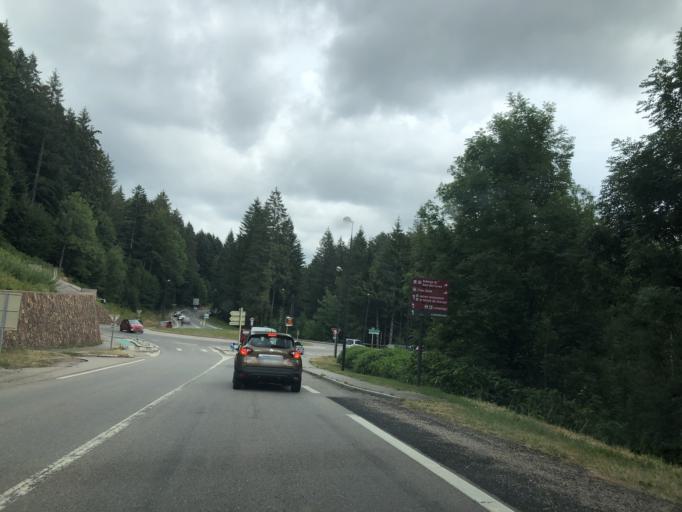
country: FR
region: Lorraine
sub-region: Departement des Vosges
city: Xonrupt-Longemer
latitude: 48.0851
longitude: 6.9089
